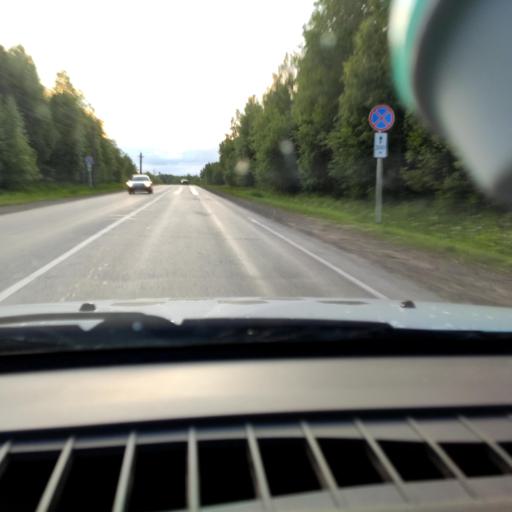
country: RU
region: Perm
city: Novyye Lyady
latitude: 58.2916
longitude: 56.6912
